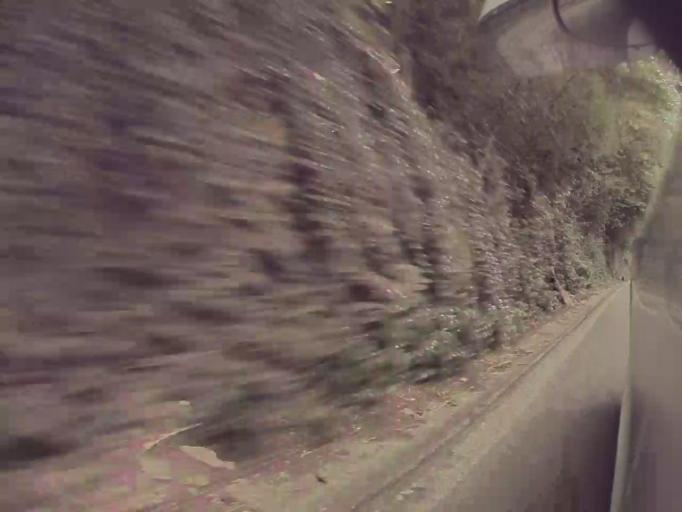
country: BE
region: Wallonia
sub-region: Province de Liege
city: Hamoir
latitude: 50.4135
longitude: 5.5082
